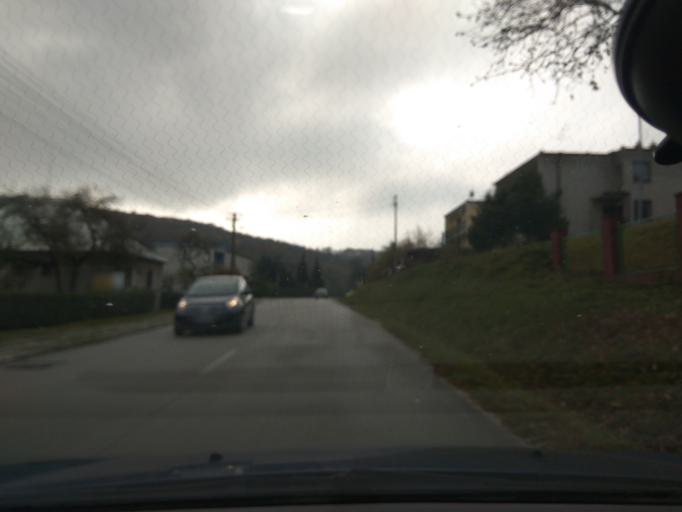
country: SK
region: Trnavsky
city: Vrbove
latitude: 48.6944
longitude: 17.6871
